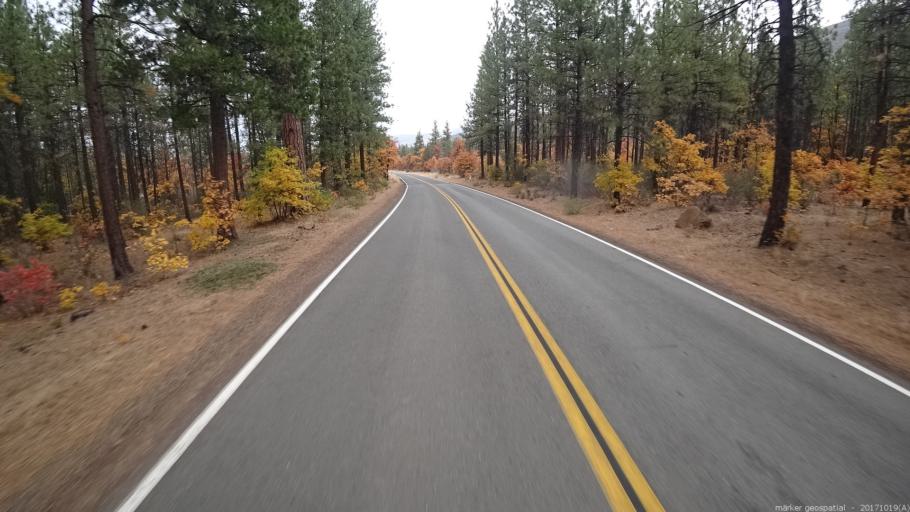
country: US
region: California
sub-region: Shasta County
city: Burney
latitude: 41.1836
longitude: -121.3629
